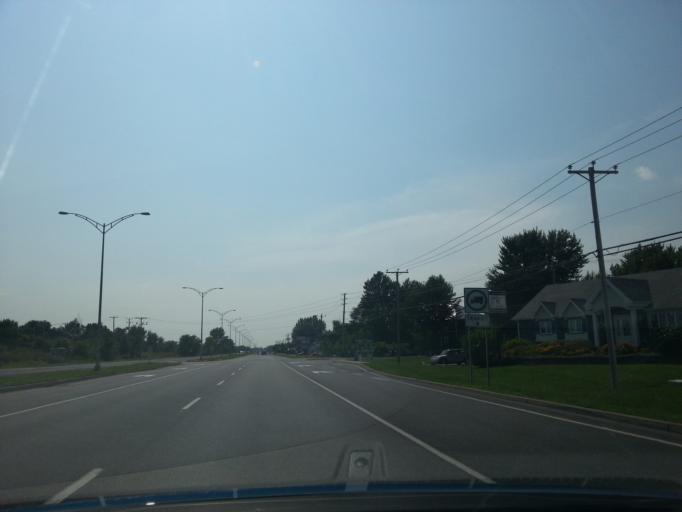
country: CA
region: Quebec
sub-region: Monteregie
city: Saint-Basile-le-Grand
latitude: 45.5316
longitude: -73.2802
